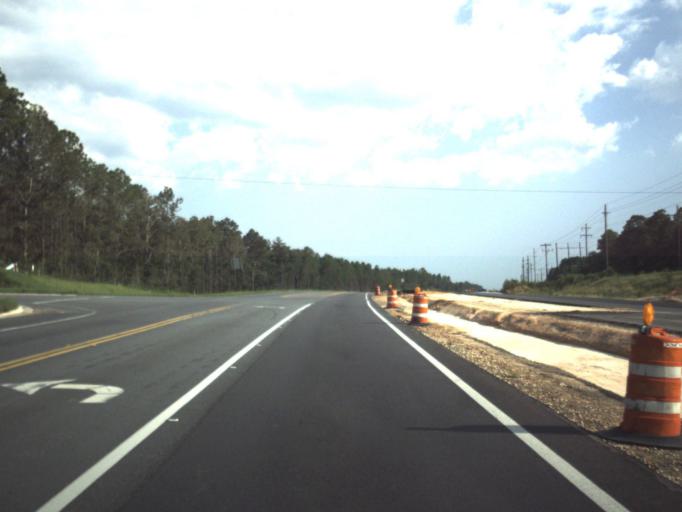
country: US
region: Florida
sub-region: Walton County
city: Freeport
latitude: 30.5993
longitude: -86.1108
